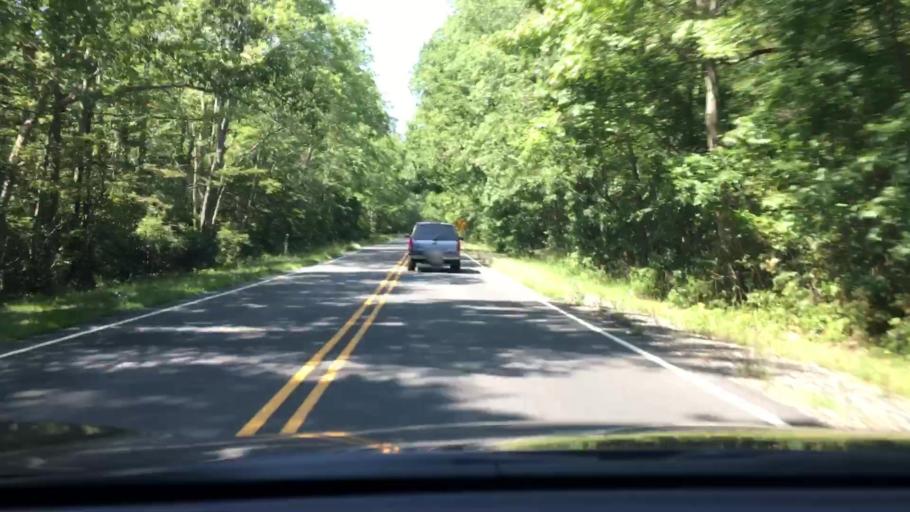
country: US
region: New Jersey
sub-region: Cape May County
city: Woodbine
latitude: 39.2593
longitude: -74.9072
